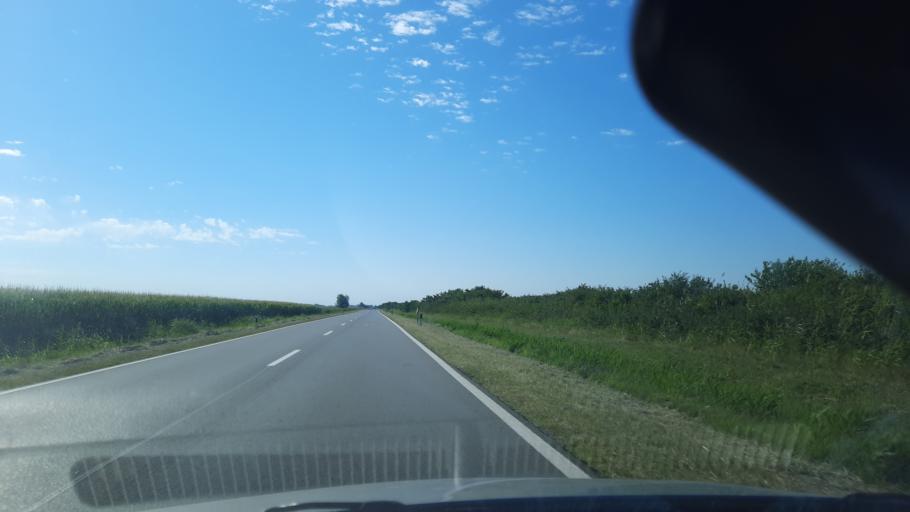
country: RS
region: Autonomna Pokrajina Vojvodina
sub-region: Juznobanatski Okrug
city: Kovin
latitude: 44.7849
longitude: 20.9245
